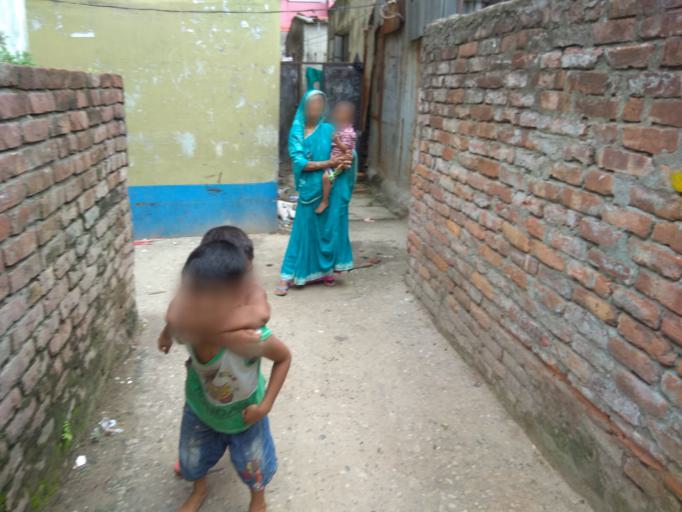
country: BD
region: Dhaka
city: Azimpur
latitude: 23.7968
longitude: 90.3754
